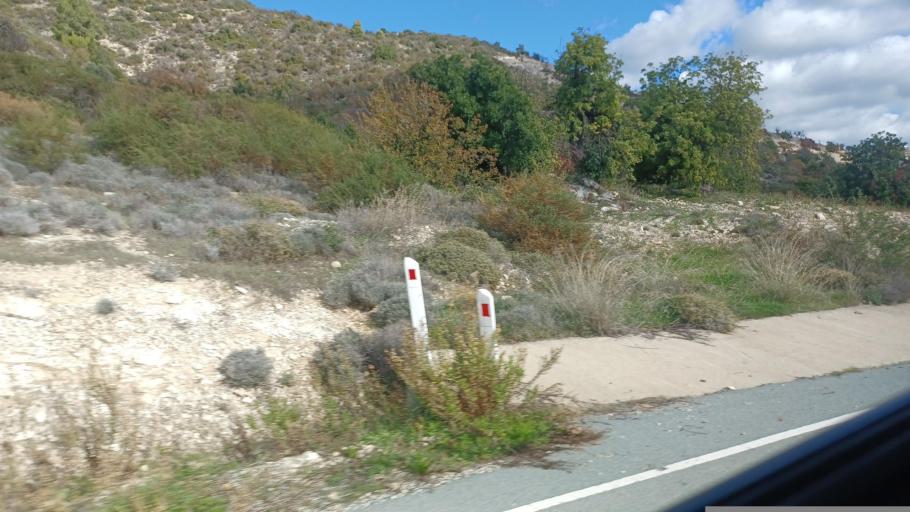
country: CY
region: Limassol
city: Pano Polemidia
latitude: 34.7935
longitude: 32.9838
